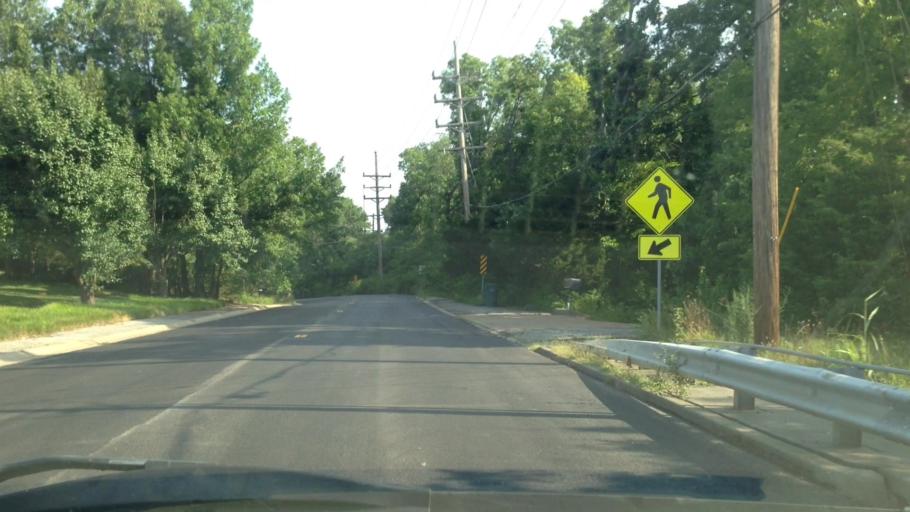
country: US
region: Missouri
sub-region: Saint Louis County
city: Des Peres
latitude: 38.5766
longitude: -90.4347
